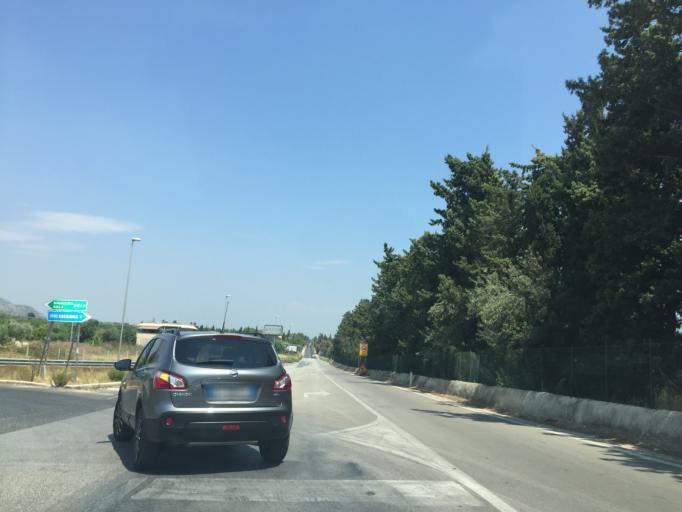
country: IT
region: Sicily
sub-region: Provincia di Siracusa
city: Avola
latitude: 36.9303
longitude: 15.1657
